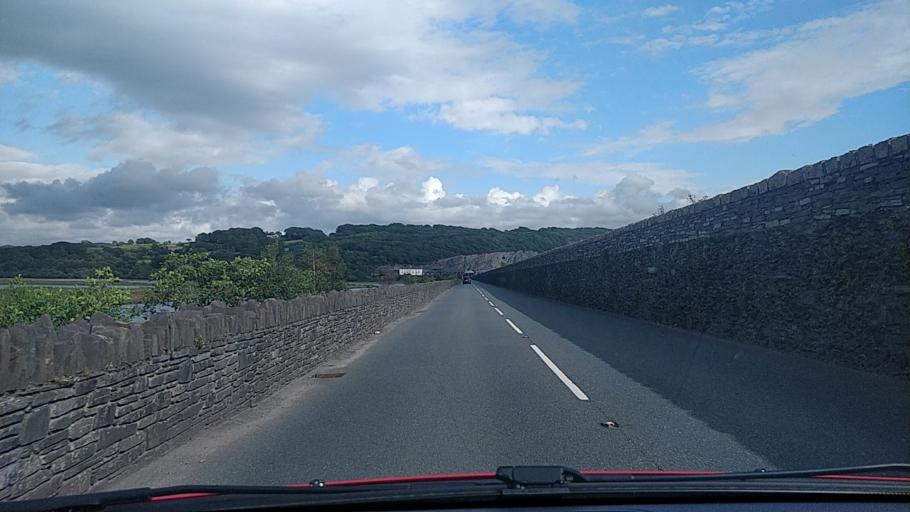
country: GB
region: Wales
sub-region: Gwynedd
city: Porthmadog
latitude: 52.9219
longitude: -4.1165
